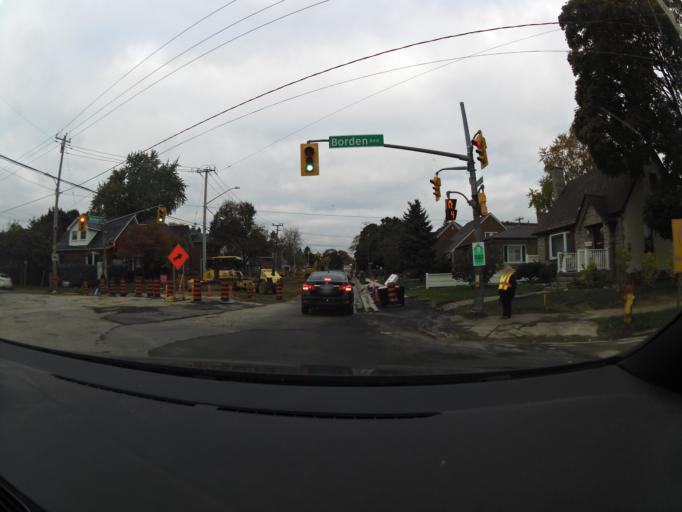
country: CA
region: Ontario
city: Kitchener
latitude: 43.4457
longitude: -80.4711
